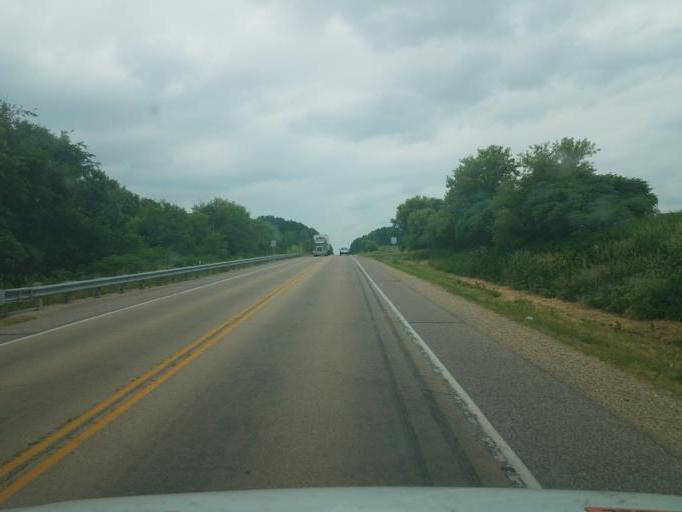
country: US
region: Wisconsin
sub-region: Sauk County
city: Reedsburg
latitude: 43.5980
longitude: -90.1296
